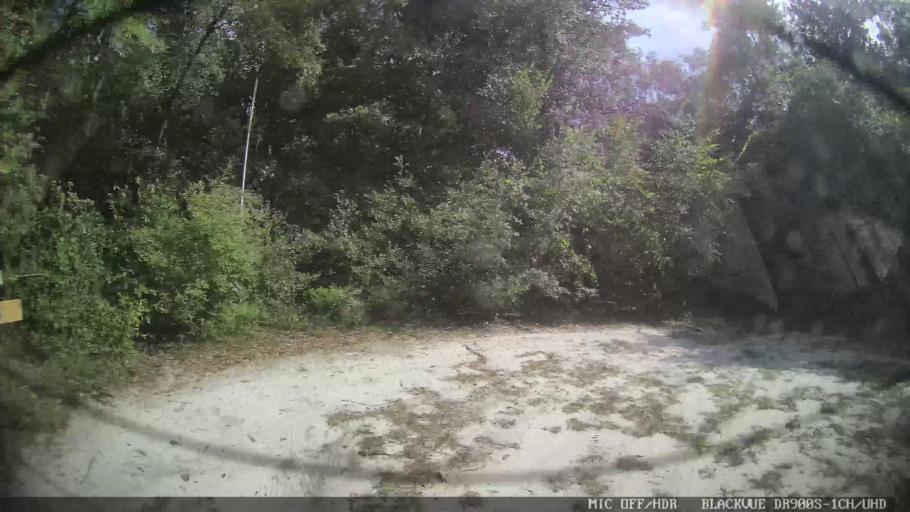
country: US
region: Florida
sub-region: Hamilton County
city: Jasper
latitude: 30.5474
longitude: -83.0824
